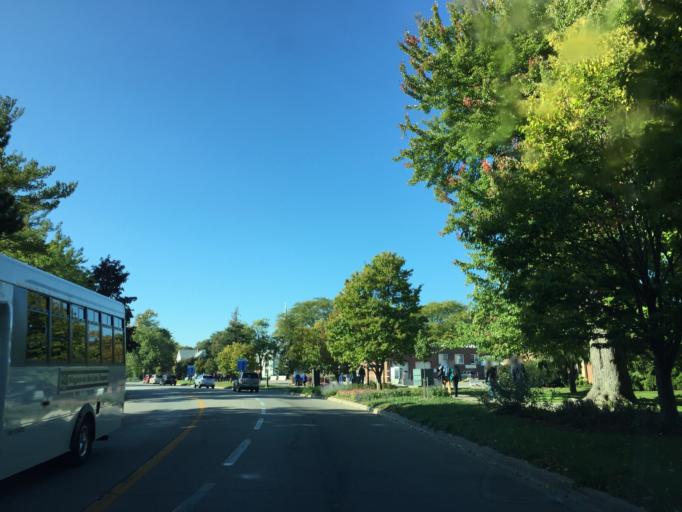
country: US
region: New York
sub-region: Niagara County
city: Youngstown
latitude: 43.2524
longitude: -79.0664
